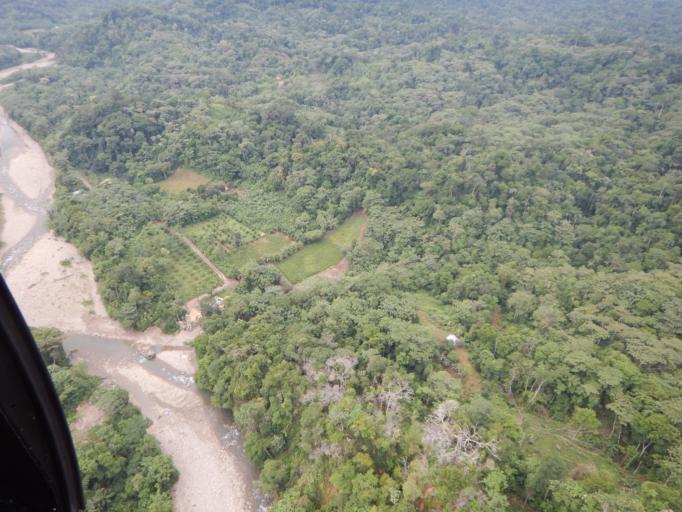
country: BO
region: Cochabamba
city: Chimore
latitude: -17.2807
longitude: -64.6293
